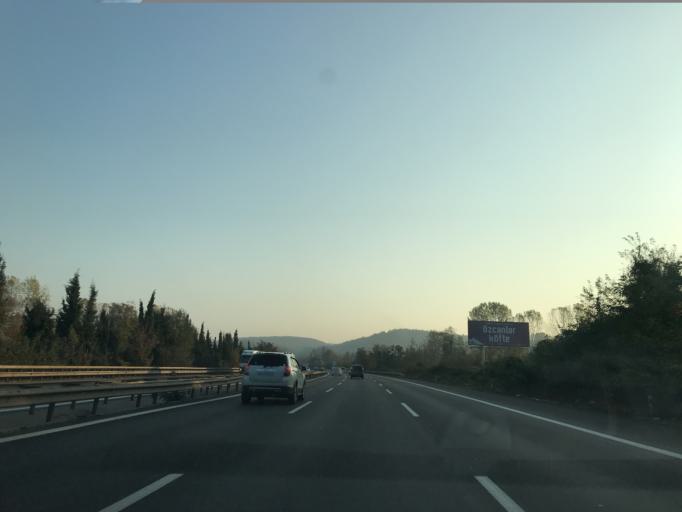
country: TR
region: Sakarya
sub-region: Merkez
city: Sapanca
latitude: 40.6979
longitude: 30.3007
